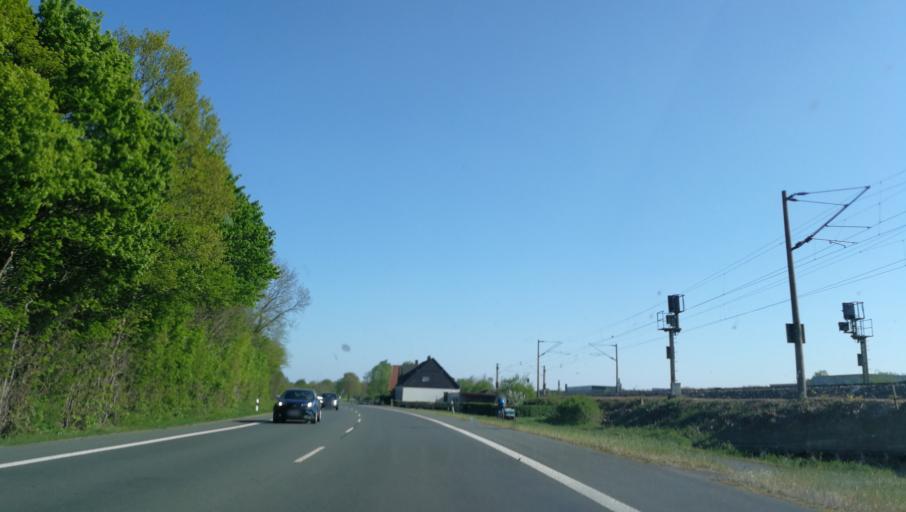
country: DE
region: North Rhine-Westphalia
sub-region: Regierungsbezirk Munster
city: Rheine
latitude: 52.2571
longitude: 7.4560
